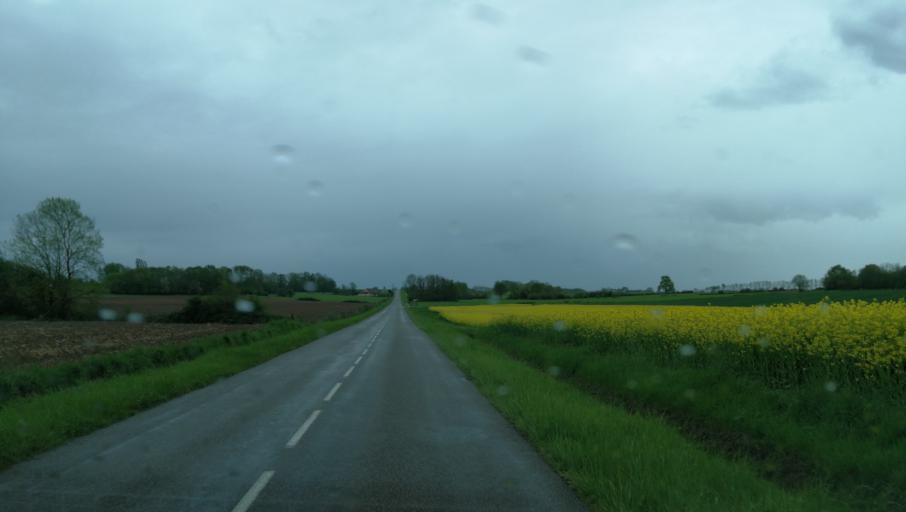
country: FR
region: Franche-Comte
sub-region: Departement du Jura
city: Bletterans
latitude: 46.8261
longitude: 5.3804
